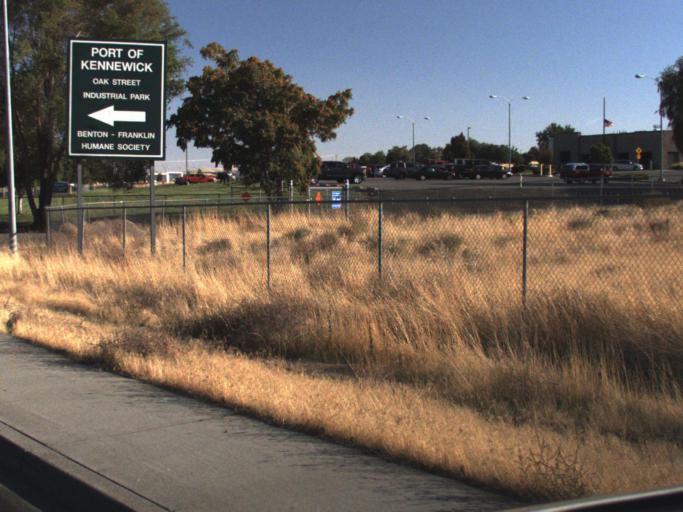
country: US
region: Washington
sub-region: Franklin County
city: Pasco
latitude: 46.2053
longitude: -119.1020
